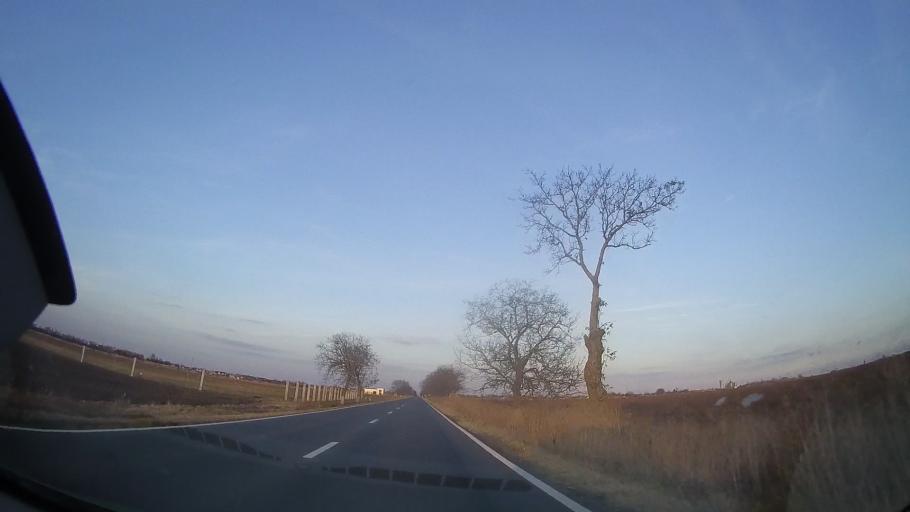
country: RO
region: Constanta
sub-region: Comuna Topraisar
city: Topraisar
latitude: 44.0029
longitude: 28.4375
